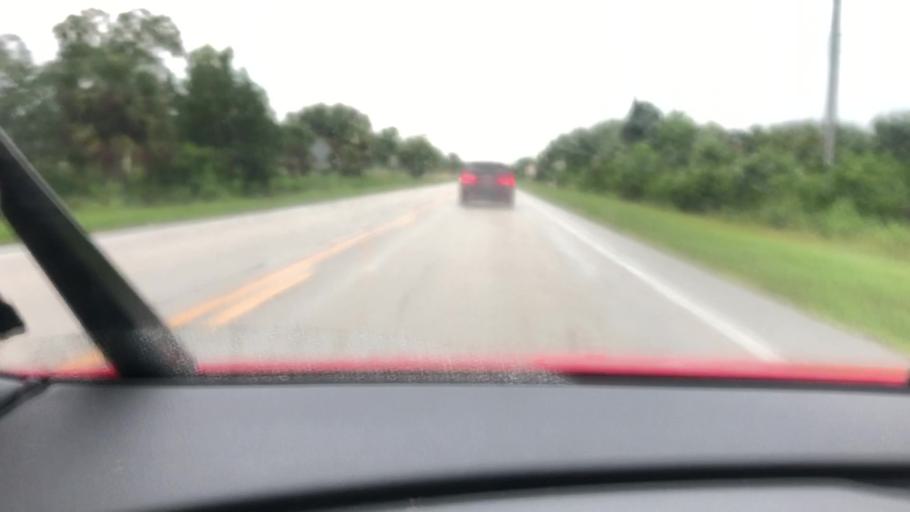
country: US
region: Florida
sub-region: Volusia County
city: Samsula-Spruce Creek
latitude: 29.0750
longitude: -81.0682
